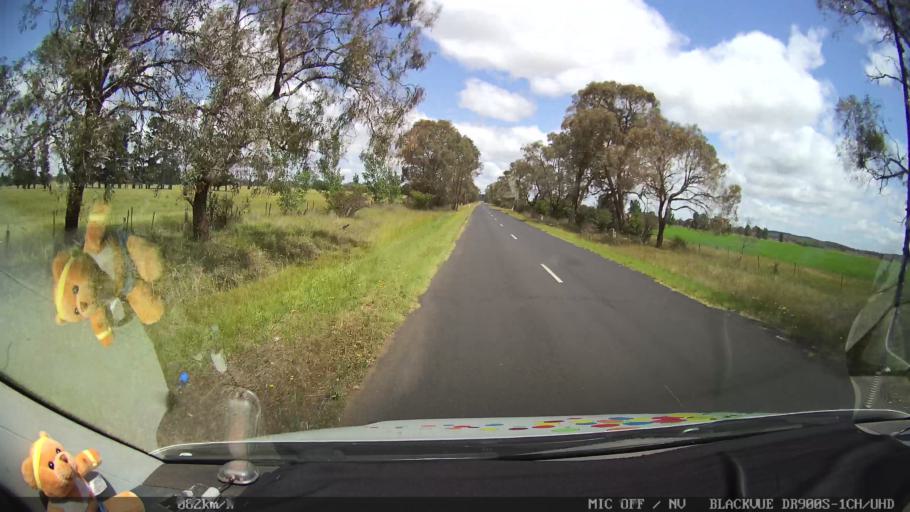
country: AU
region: New South Wales
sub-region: Glen Innes Severn
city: Glen Innes
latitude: -29.6353
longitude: 151.6819
